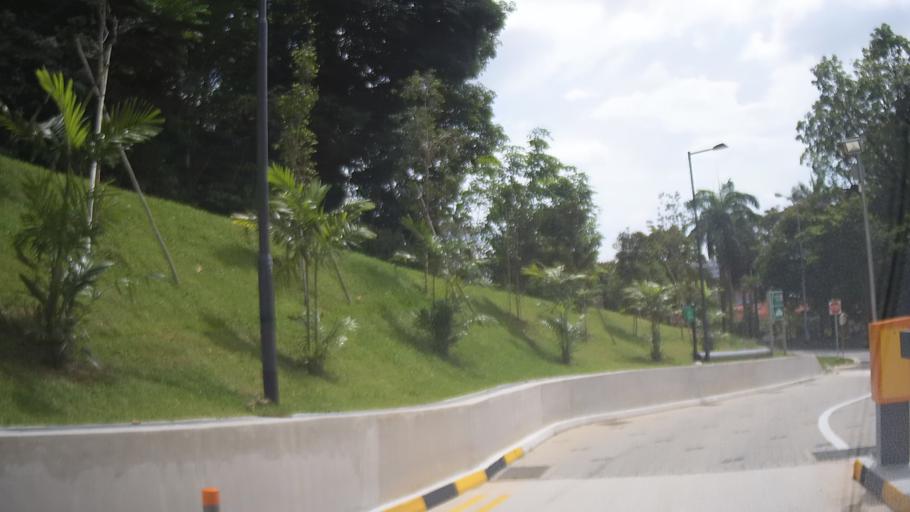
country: MY
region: Johor
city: Johor Bahru
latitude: 1.4355
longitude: 103.7778
